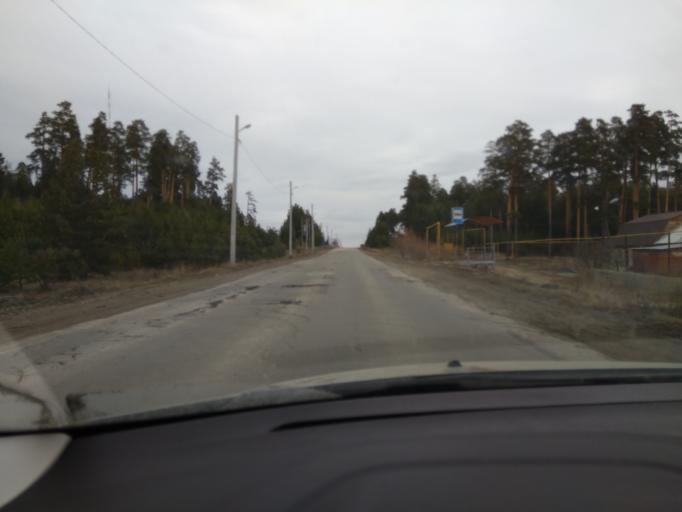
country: RU
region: Chelyabinsk
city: Kyshtym
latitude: 55.6958
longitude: 60.5078
